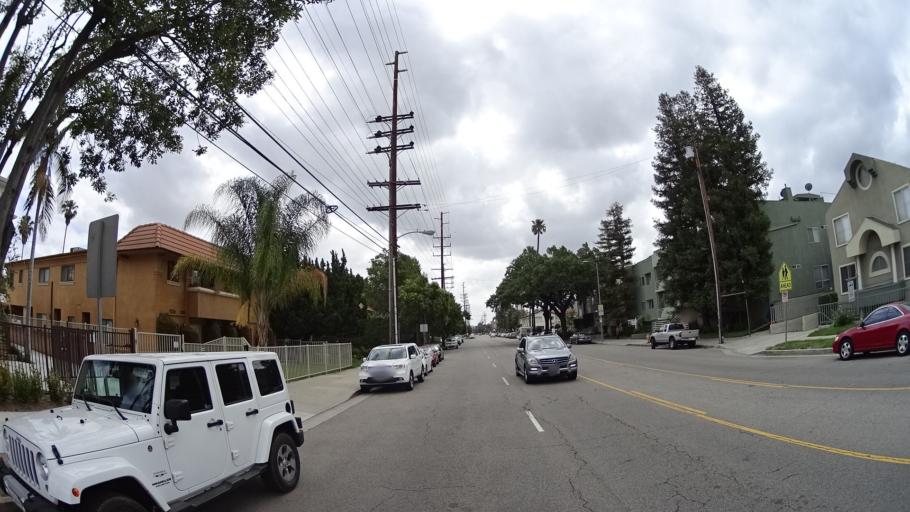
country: US
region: California
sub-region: Los Angeles County
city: Universal City
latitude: 34.1505
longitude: -118.3694
